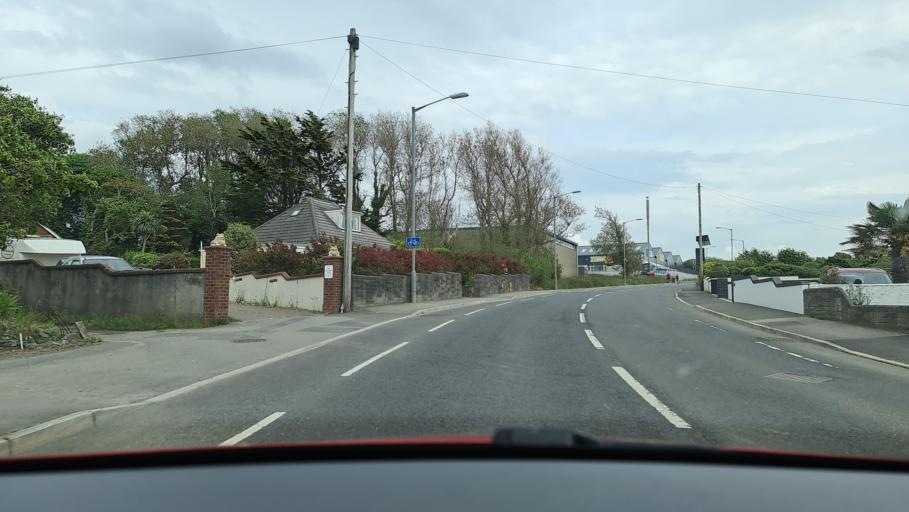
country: GB
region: England
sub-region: Cornwall
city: Bude
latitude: 50.8207
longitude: -4.5348
